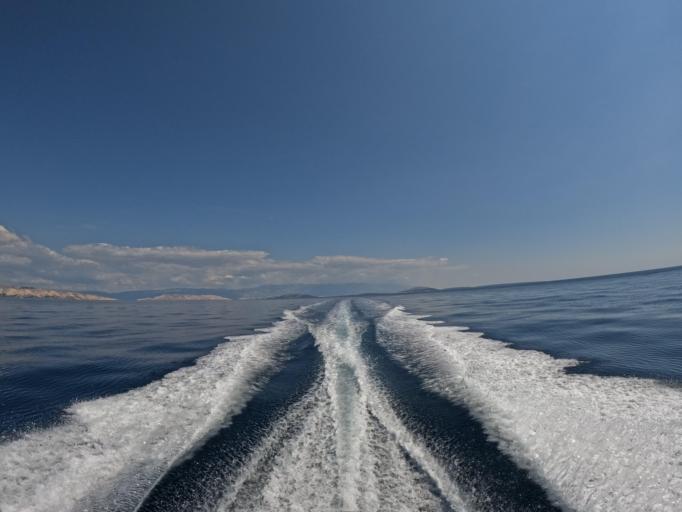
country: HR
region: Primorsko-Goranska
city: Punat
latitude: 44.9137
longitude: 14.5830
